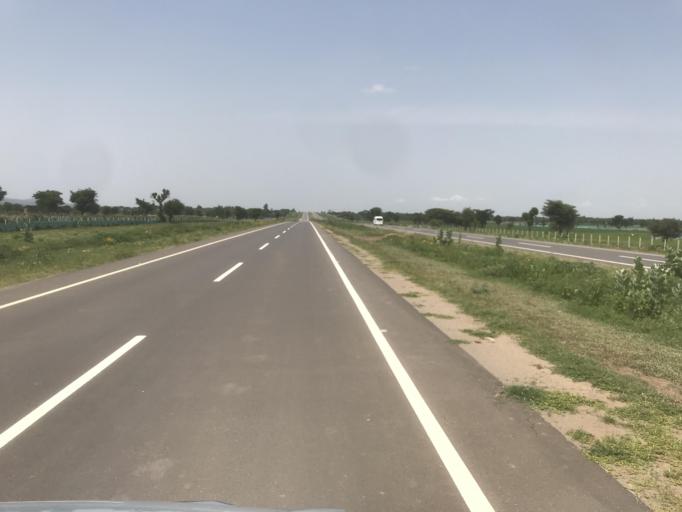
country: ET
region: Oromiya
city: Mojo
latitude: 8.3753
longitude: 38.9999
